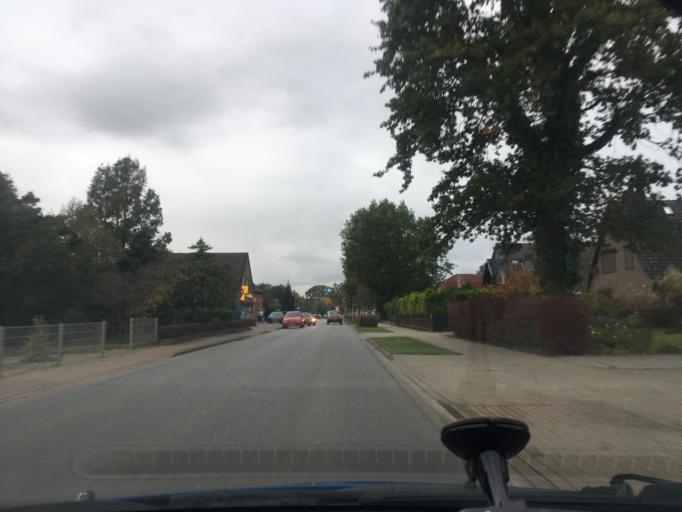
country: DE
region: Lower Saxony
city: Marschacht
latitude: 53.4157
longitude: 10.3733
